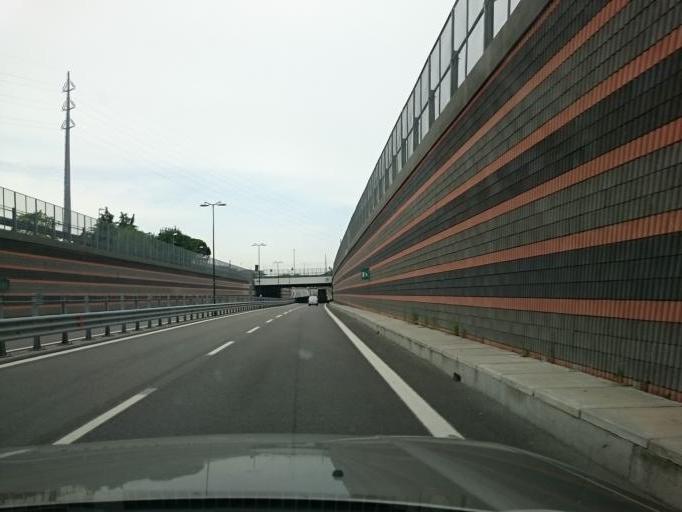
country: IT
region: Veneto
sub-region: Provincia di Venezia
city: Campalto
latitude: 45.5011
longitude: 12.2734
